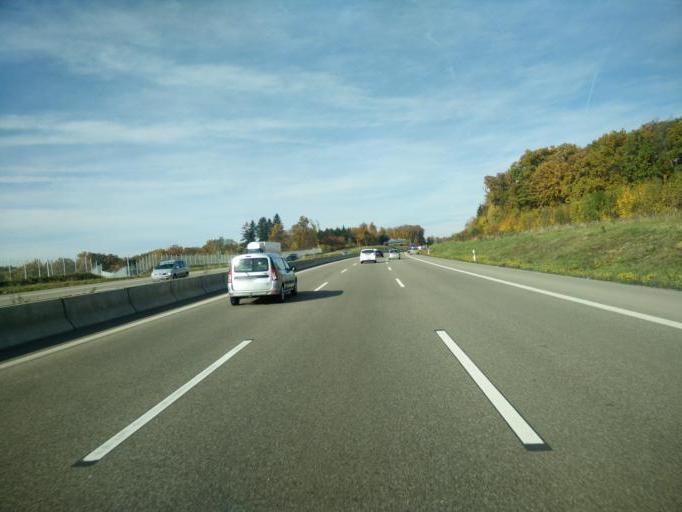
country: DE
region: Baden-Wuerttemberg
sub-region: Karlsruhe Region
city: Heimsheim
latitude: 48.8298
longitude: 8.8669
